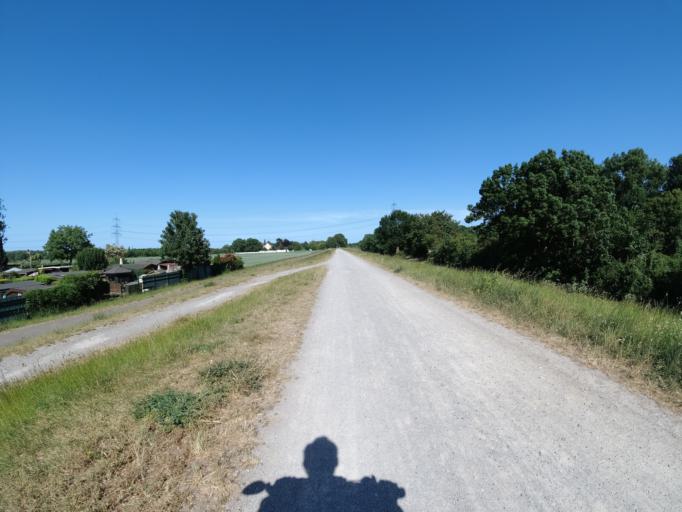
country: DE
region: North Rhine-Westphalia
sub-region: Regierungsbezirk Dusseldorf
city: Hochfeld
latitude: 51.3788
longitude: 6.6898
